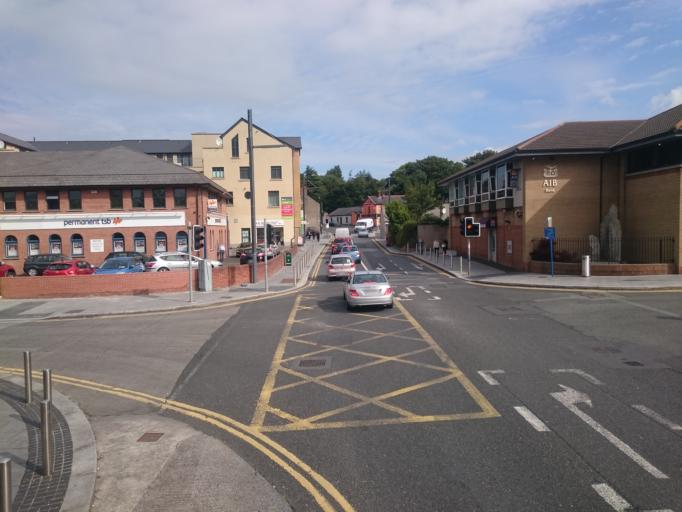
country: IE
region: Leinster
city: Tallaght
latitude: 53.2869
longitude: -6.3621
